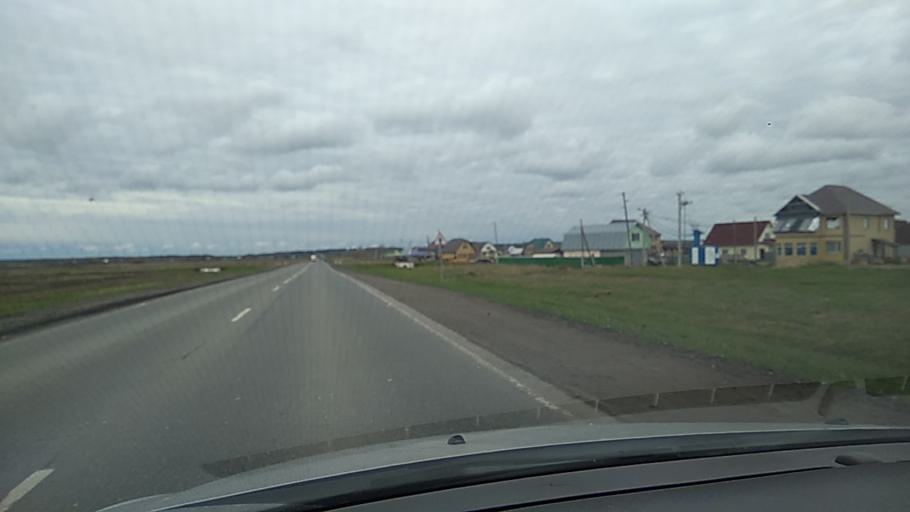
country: RU
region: Tjumen
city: Chervishevo
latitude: 56.9270
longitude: 65.4255
